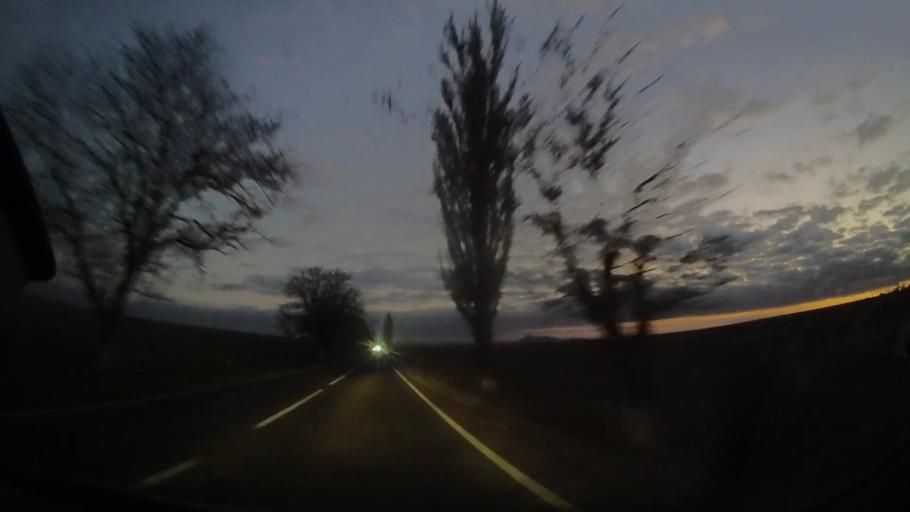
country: RO
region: Tulcea
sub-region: Comuna Frecatei
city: Cataloi
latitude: 45.0900
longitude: 28.7410
